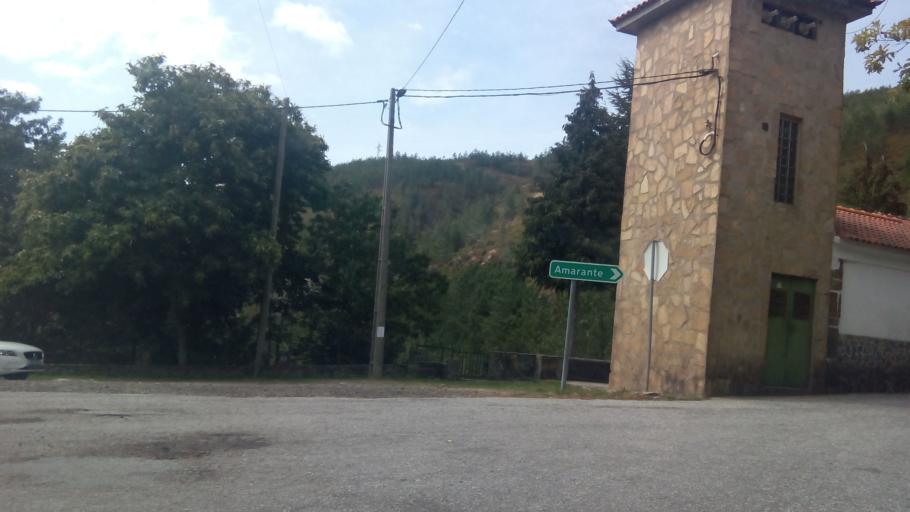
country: PT
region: Vila Real
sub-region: Mesao Frio
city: Mesao Frio
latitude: 41.2758
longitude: -7.9326
